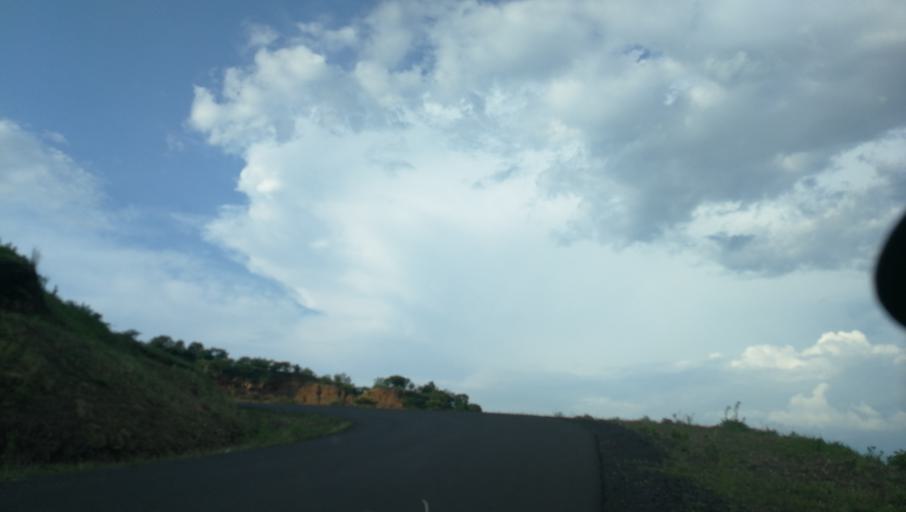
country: ET
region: Southern Nations, Nationalities, and People's Region
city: Areka
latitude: 6.8465
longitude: 37.2757
